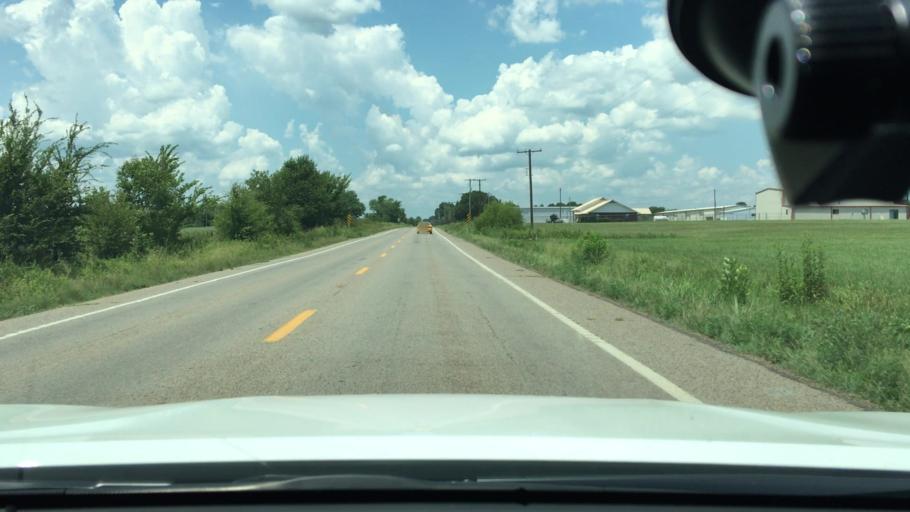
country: US
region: Arkansas
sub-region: Logan County
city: Booneville
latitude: 35.1478
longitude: -93.8630
